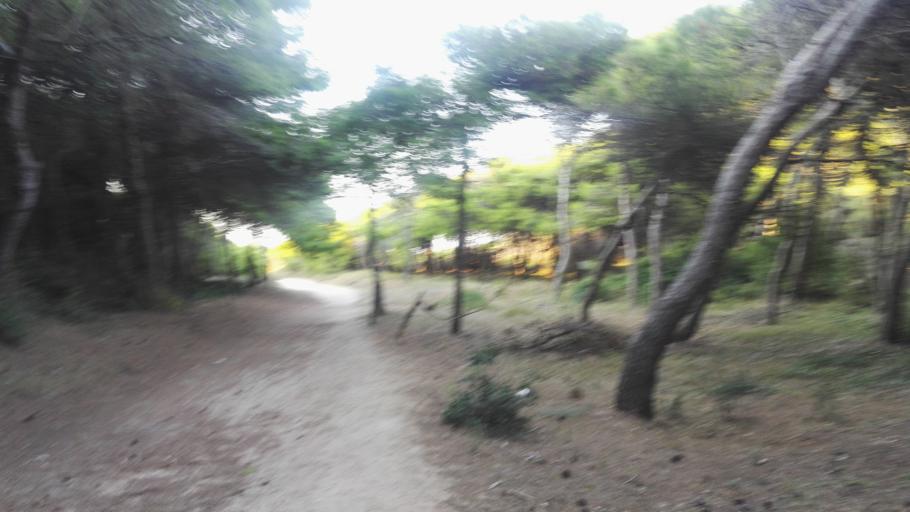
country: IT
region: Apulia
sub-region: Provincia di Lecce
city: Borgagne
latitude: 40.2674
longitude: 18.4355
